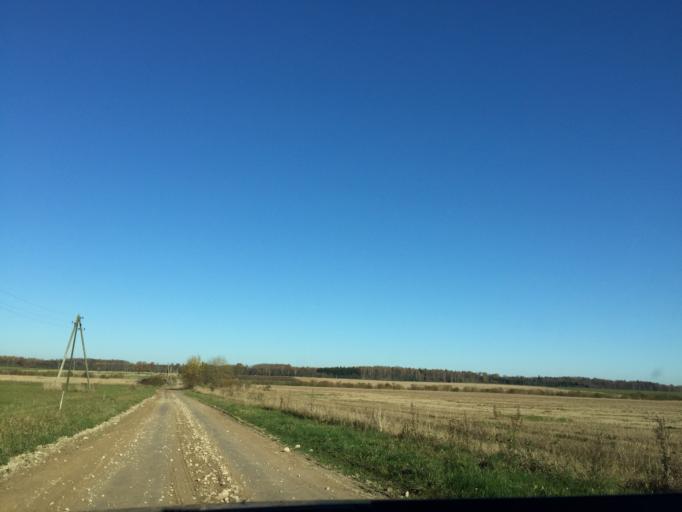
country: LV
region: Aizkraukles Rajons
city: Aizkraukle
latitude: 56.6532
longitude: 25.2048
